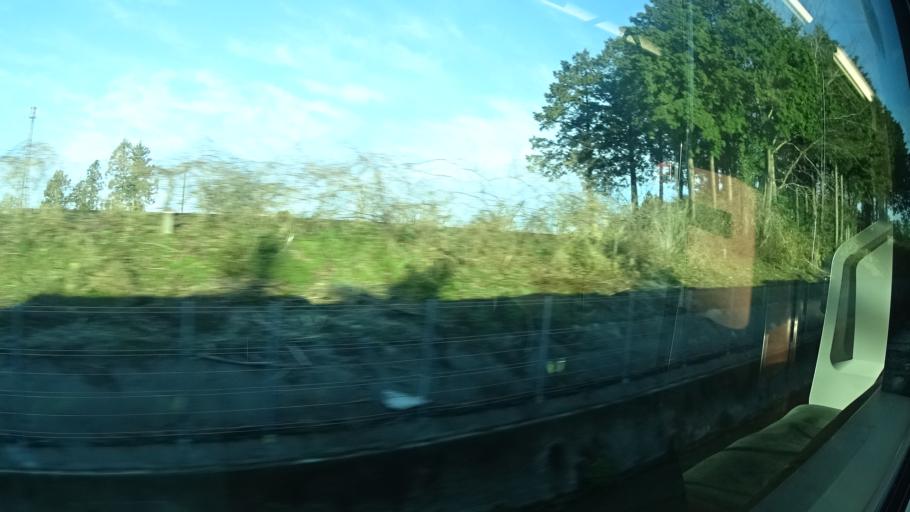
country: JP
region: Fukushima
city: Namie
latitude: 37.3971
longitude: 140.9867
